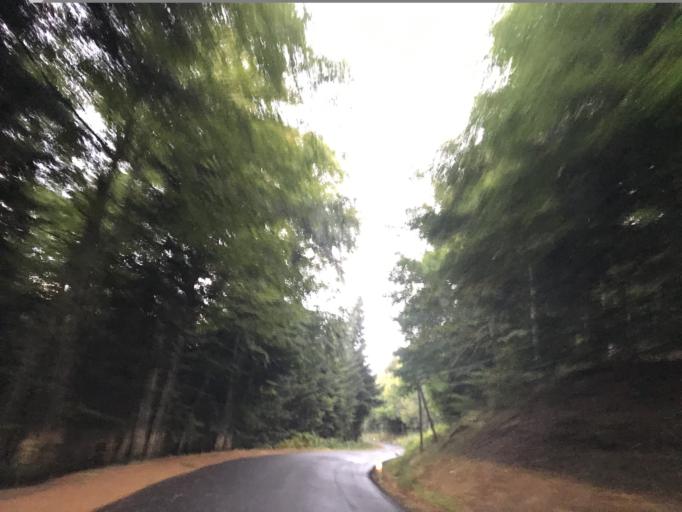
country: FR
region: Auvergne
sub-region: Departement du Puy-de-Dome
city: Celles-sur-Durolle
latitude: 45.8101
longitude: 3.6623
